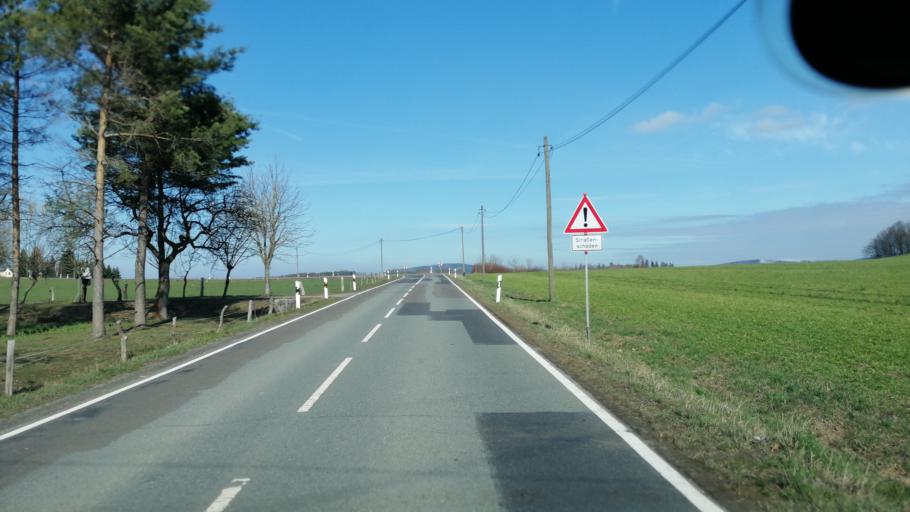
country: DE
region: Saxony
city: Schonbach
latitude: 51.0701
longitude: 14.5523
